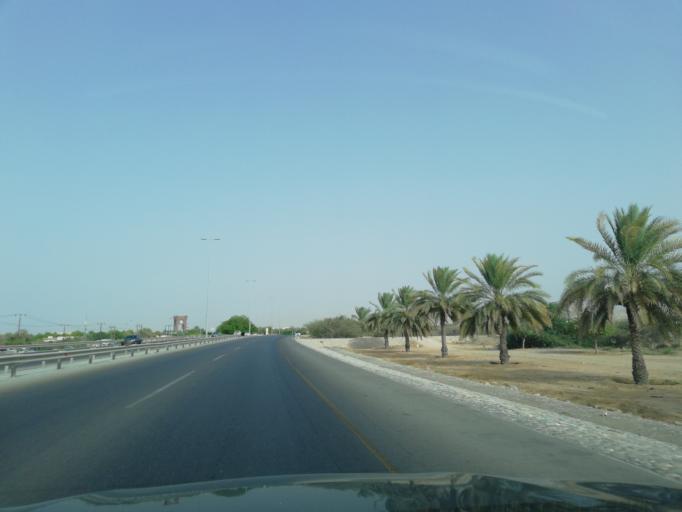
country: OM
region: Muhafazat Masqat
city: As Sib al Jadidah
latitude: 23.5890
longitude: 58.2447
